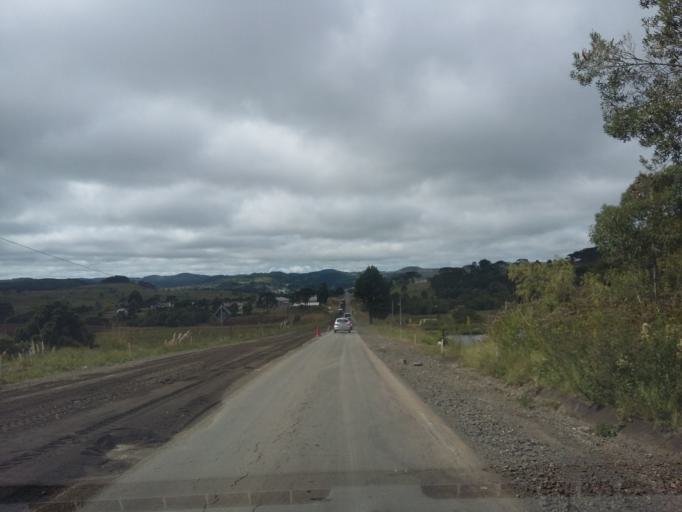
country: BR
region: Santa Catarina
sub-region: Lages
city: Lages
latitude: -27.9012
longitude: -50.1218
